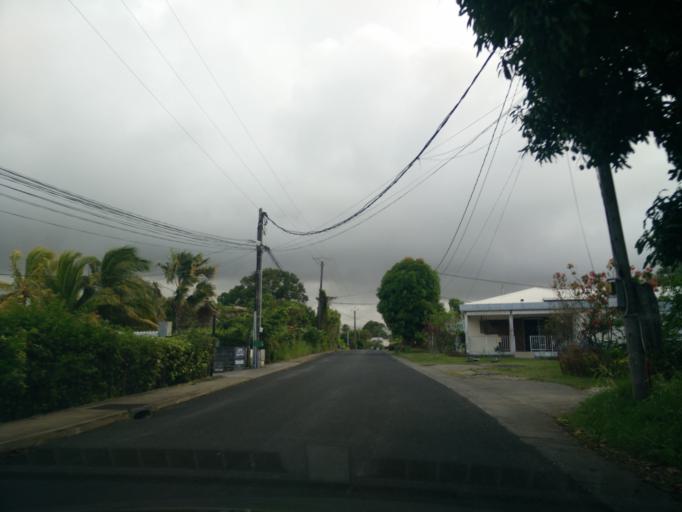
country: GP
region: Guadeloupe
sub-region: Guadeloupe
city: Petit-Bourg
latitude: 16.1894
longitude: -61.6122
